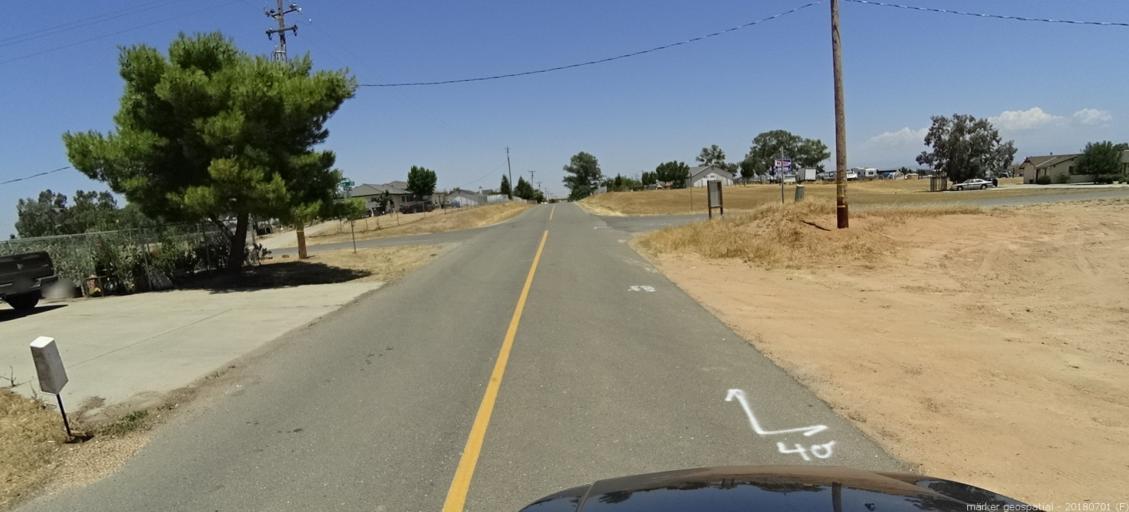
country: US
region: California
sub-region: Madera County
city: Madera Acres
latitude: 37.0393
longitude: -119.9957
